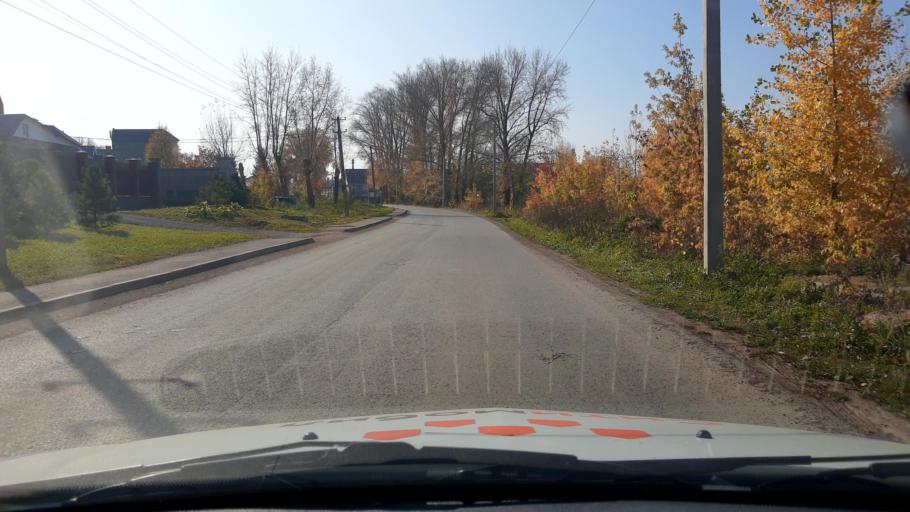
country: RU
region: Bashkortostan
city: Ufa
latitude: 54.6905
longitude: 55.9625
